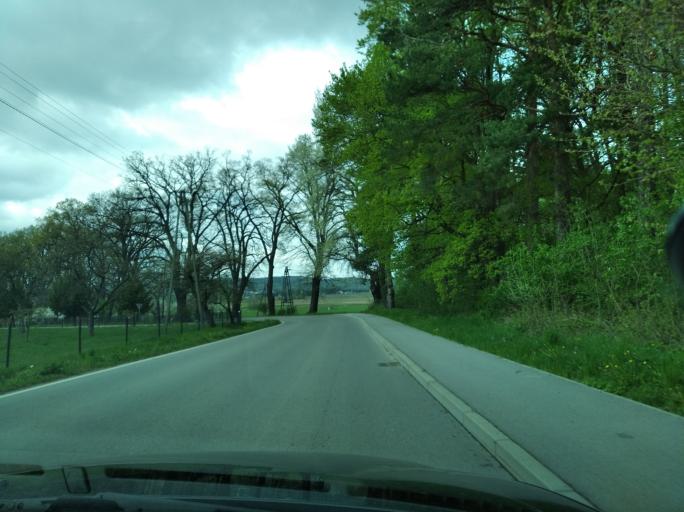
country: PL
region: Subcarpathian Voivodeship
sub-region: Powiat brzozowski
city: Turze Pole
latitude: 49.6445
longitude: 21.9987
